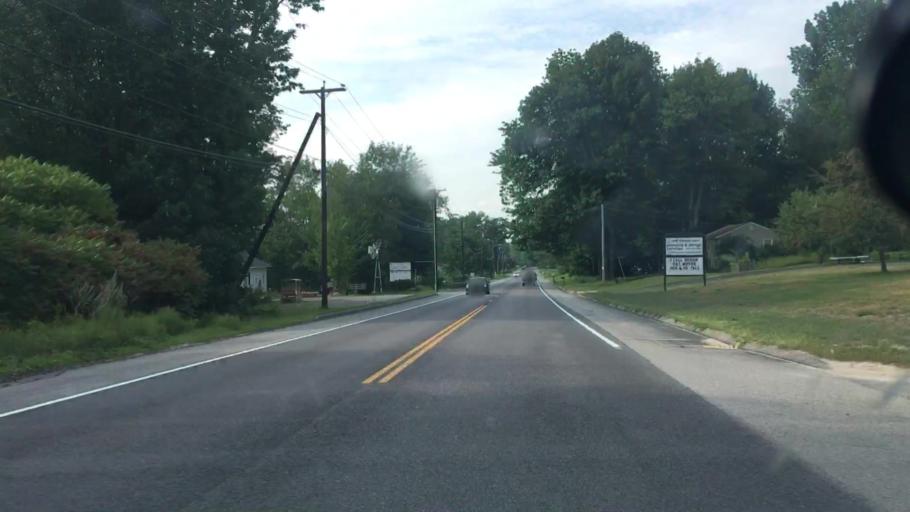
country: US
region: Maine
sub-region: Cumberland County
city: South Windham
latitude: 43.7690
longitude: -70.3779
